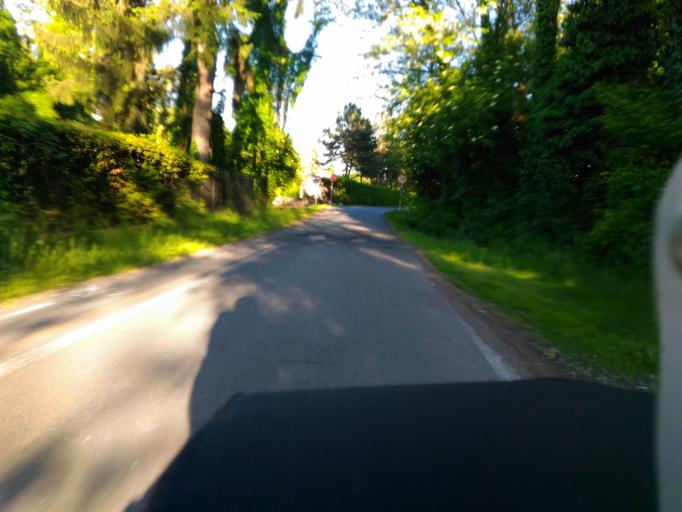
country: IT
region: Lombardy
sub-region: Provincia di Lodi
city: Lodi
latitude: 45.3088
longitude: 9.4765
